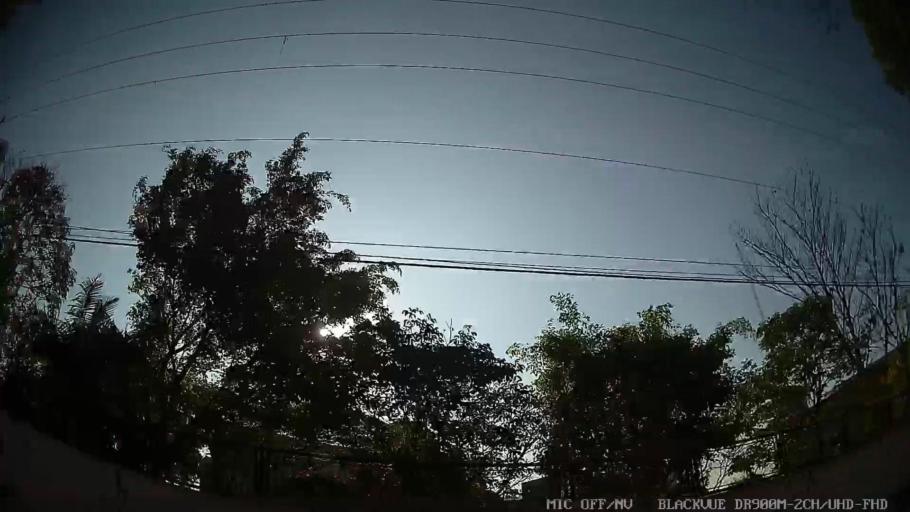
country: BR
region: Sao Paulo
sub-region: Ferraz De Vasconcelos
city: Ferraz de Vasconcelos
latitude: -23.5522
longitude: -46.4367
